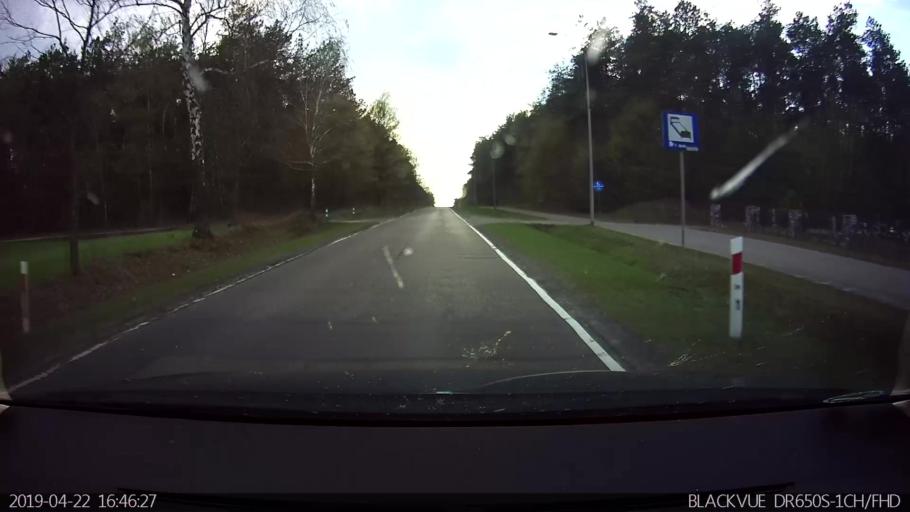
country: PL
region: Podlasie
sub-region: Powiat siemiatycki
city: Siemiatycze
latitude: 52.4359
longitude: 22.9012
